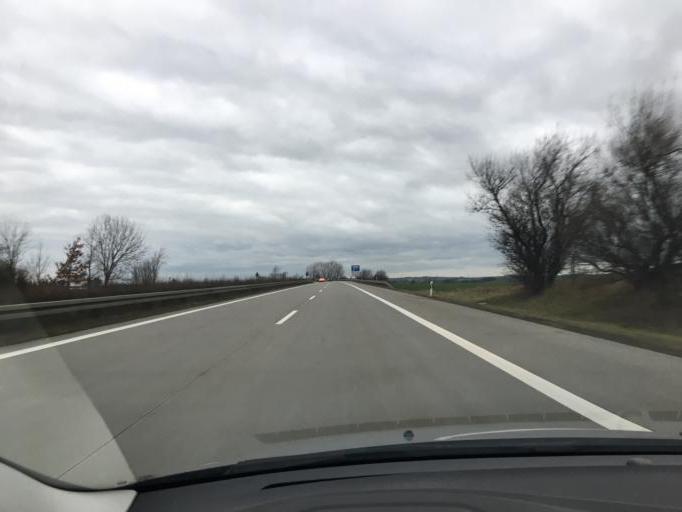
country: DE
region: Saxony
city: Nossen
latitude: 51.0759
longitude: 13.3078
